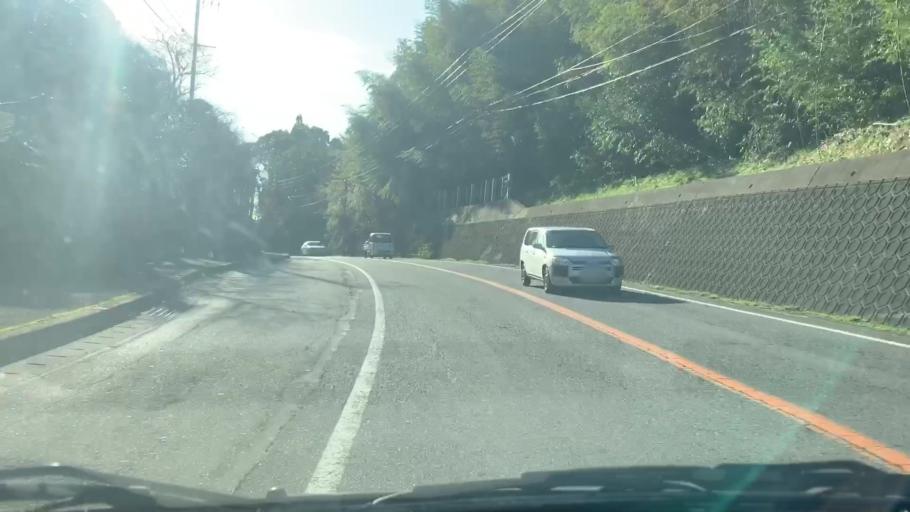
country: JP
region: Saga Prefecture
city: Takeocho-takeo
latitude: 33.2388
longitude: 130.0112
